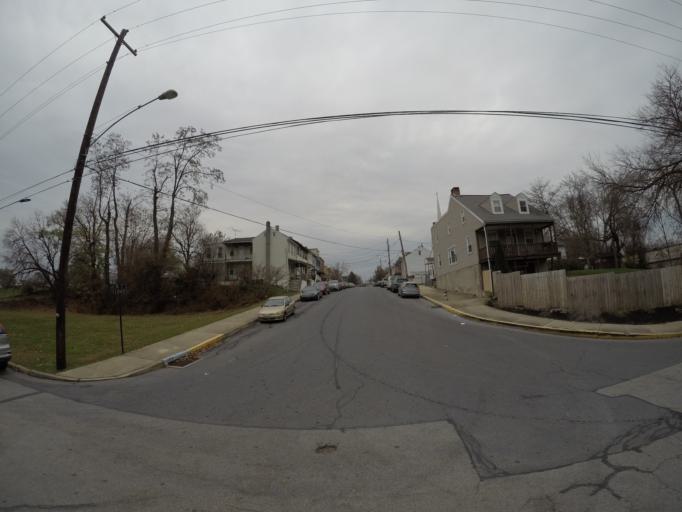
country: US
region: Pennsylvania
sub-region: Lancaster County
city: Columbia
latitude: 40.0285
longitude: -76.4960
